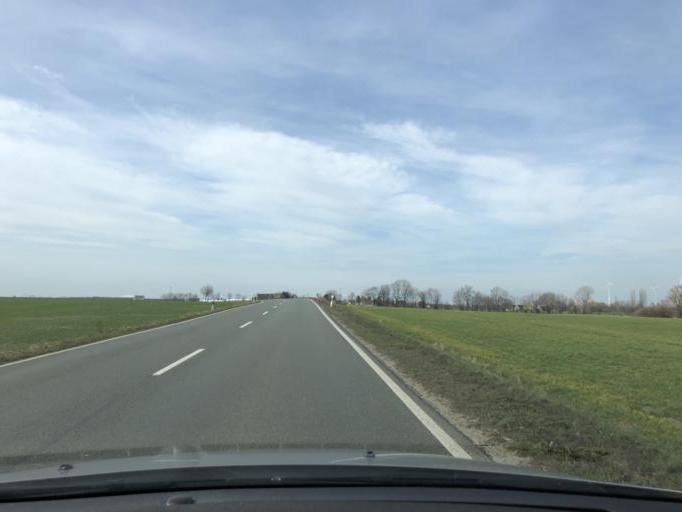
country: DE
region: Saxony-Anhalt
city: Osterfeld
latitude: 51.0825
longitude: 11.9778
